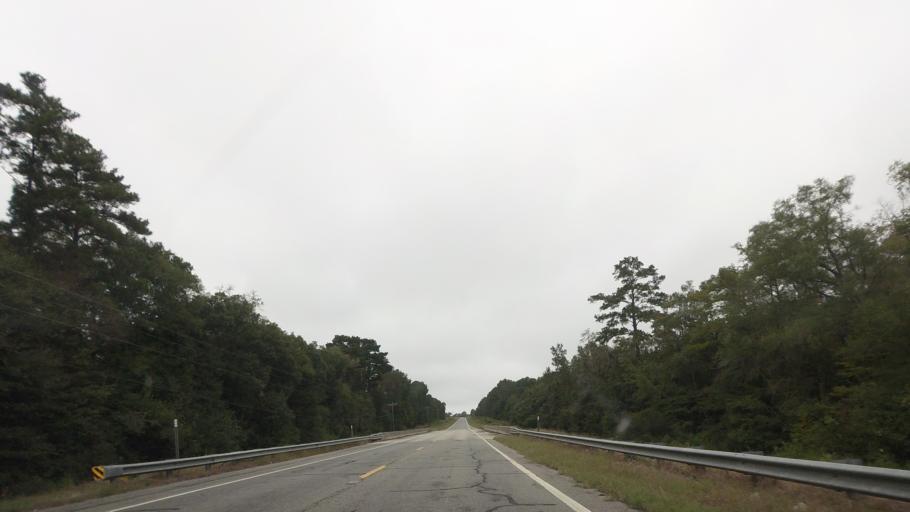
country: US
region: Georgia
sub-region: Irwin County
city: Ocilla
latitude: 31.4993
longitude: -83.2387
